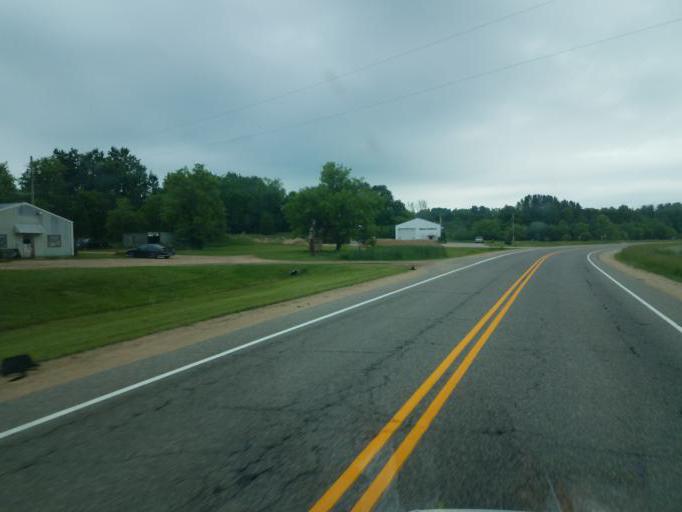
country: US
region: Wisconsin
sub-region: Juneau County
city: Elroy
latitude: 43.7626
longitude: -90.2632
